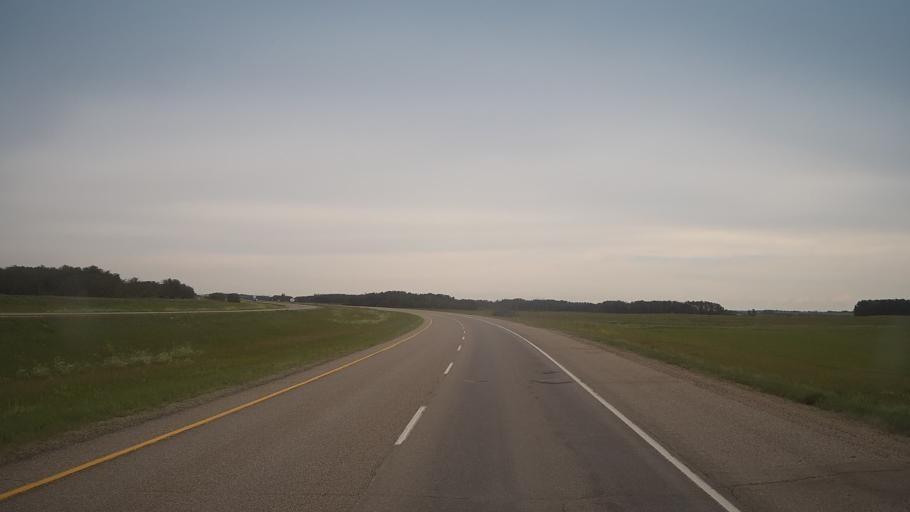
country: CA
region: Saskatchewan
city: Saskatoon
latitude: 51.8660
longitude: -106.5064
